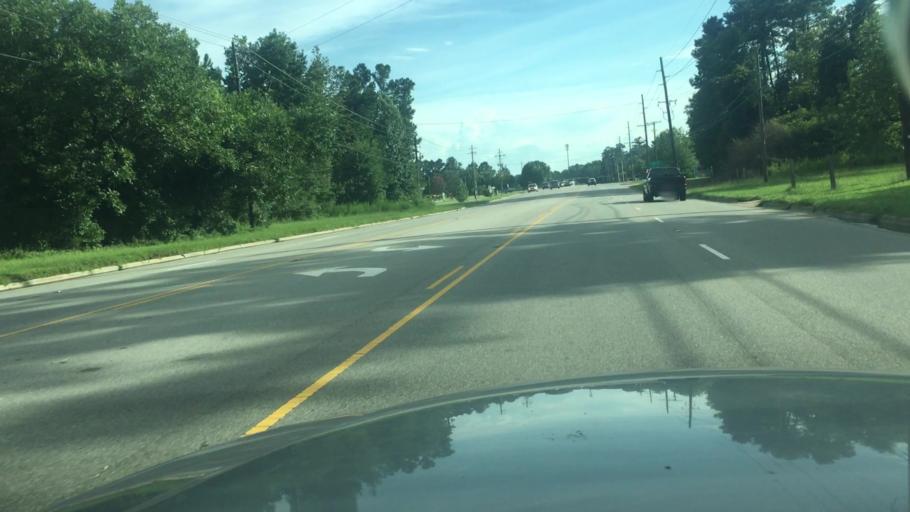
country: US
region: North Carolina
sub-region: Cumberland County
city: Eastover
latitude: 35.1651
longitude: -78.8645
